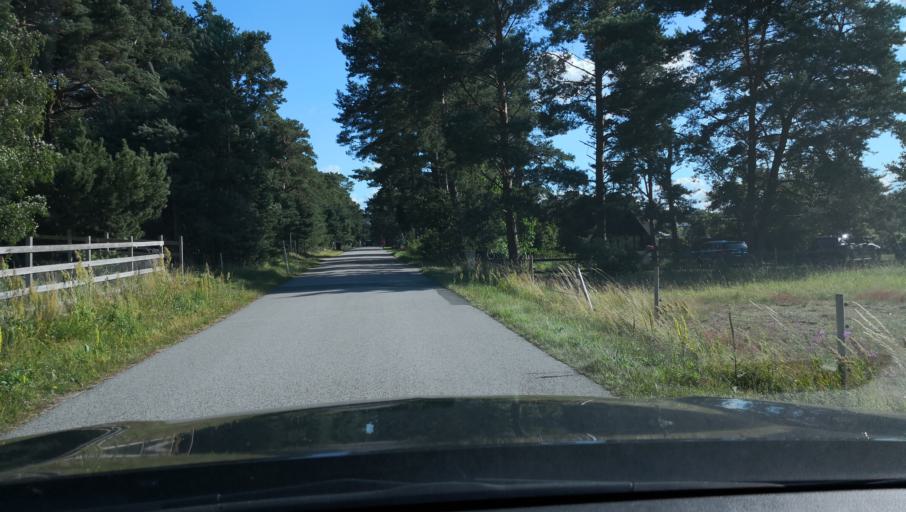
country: SE
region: Skane
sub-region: Simrishamns Kommun
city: Kivik
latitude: 55.7725
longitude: 14.1966
